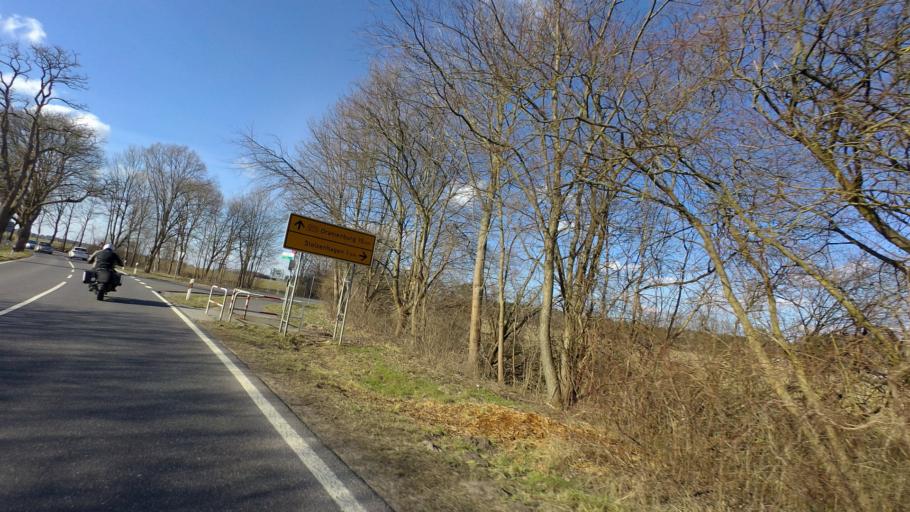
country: DE
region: Brandenburg
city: Wandlitz
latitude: 52.7508
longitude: 13.4277
